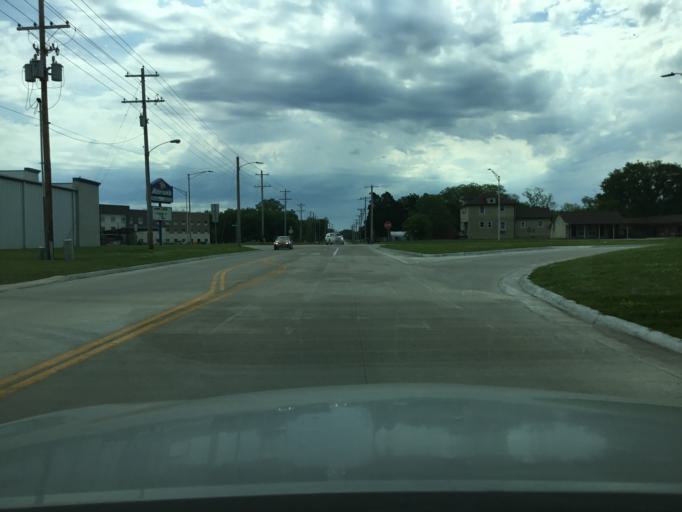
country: US
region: Kansas
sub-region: Montgomery County
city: Coffeyville
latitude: 37.0360
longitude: -95.6011
